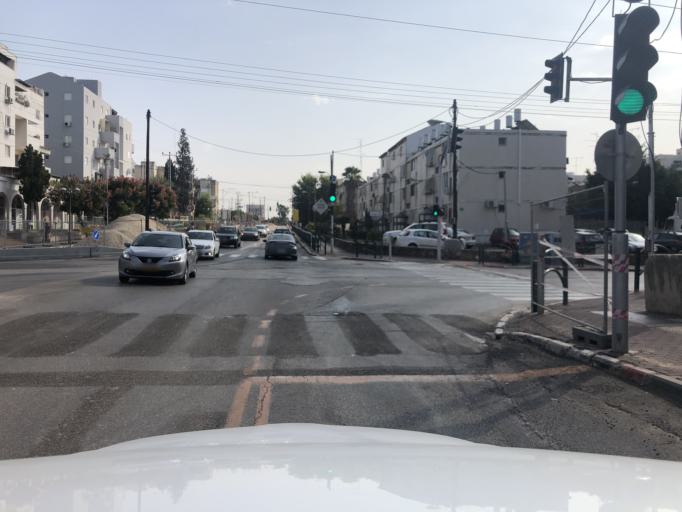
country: IL
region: Central District
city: Kfar Saba
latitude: 32.1728
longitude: 34.9191
